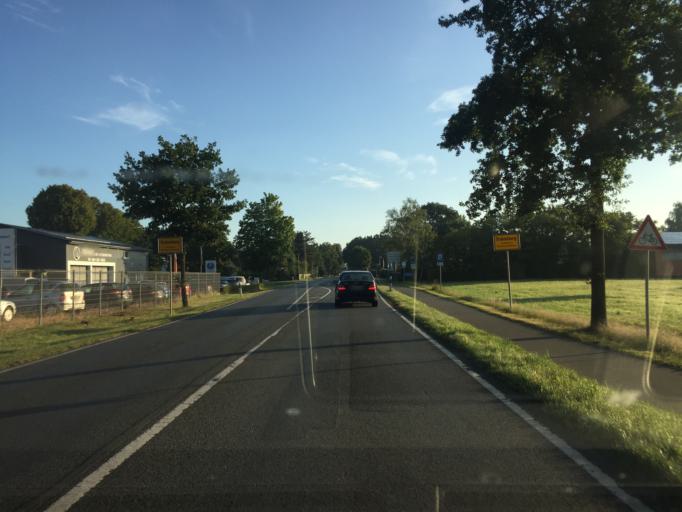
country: DE
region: Lower Saxony
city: Drakenburg
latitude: 52.6880
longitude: 9.2329
